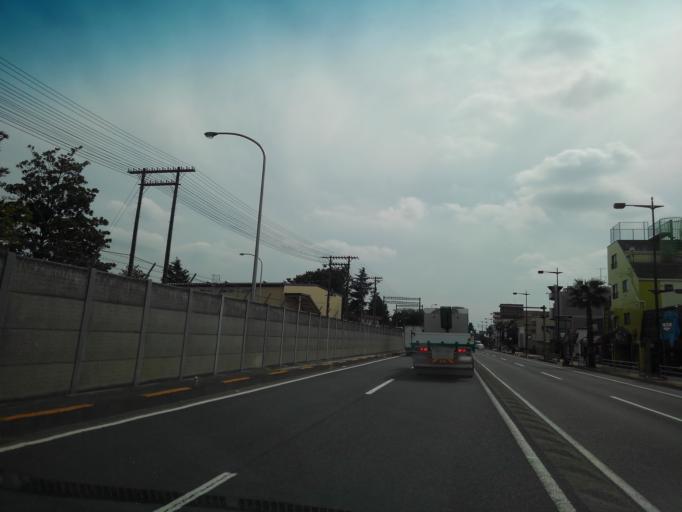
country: JP
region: Tokyo
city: Fussa
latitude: 35.7356
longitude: 139.3403
